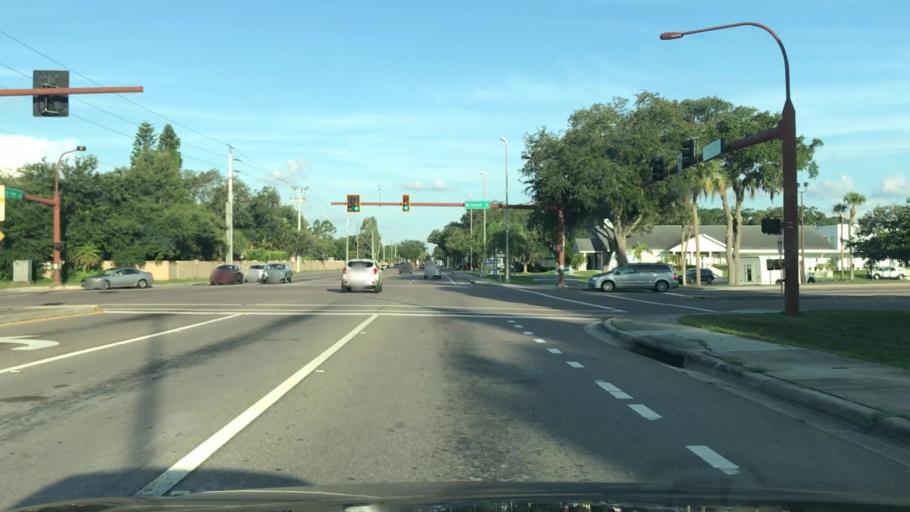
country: US
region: Florida
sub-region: Sarasota County
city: Sarasota Springs
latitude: 27.3231
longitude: -82.4825
